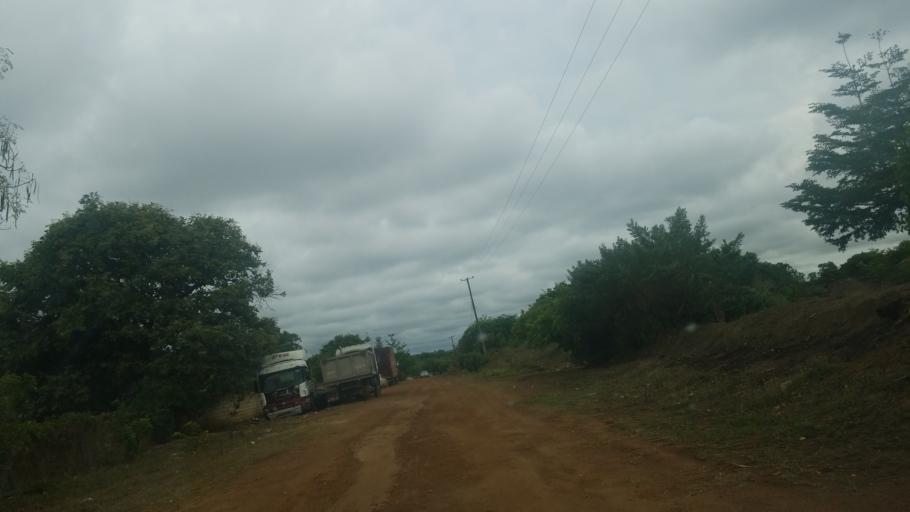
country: ZM
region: Luapula
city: Mansa
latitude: -11.1948
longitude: 28.9009
